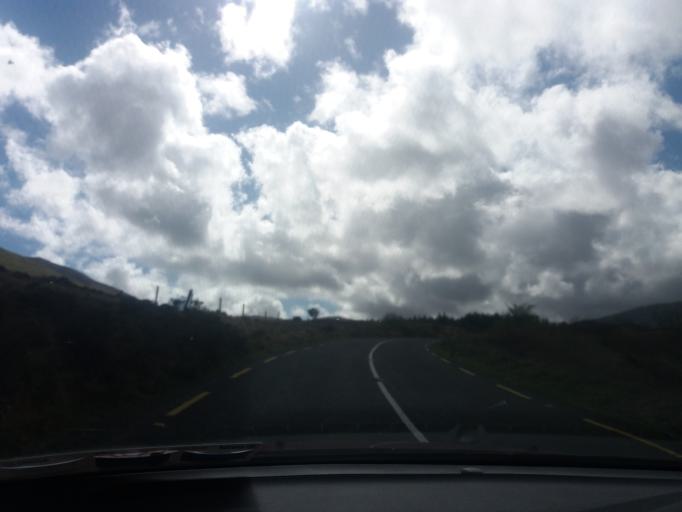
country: IE
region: Munster
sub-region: Ciarrai
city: Dingle
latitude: 52.2073
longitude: -10.1683
